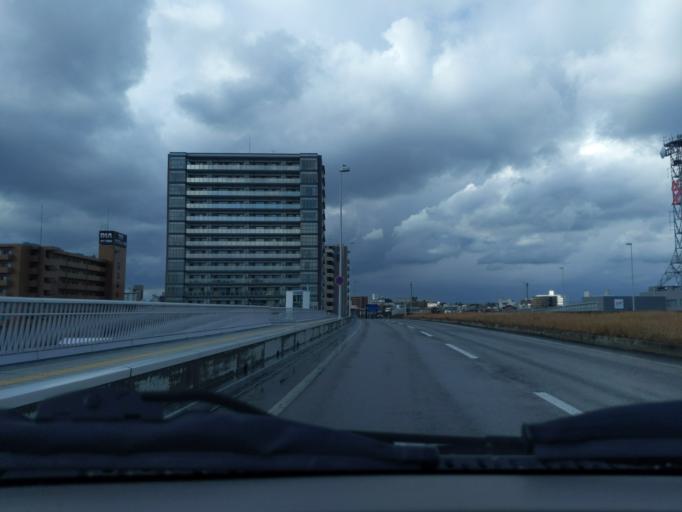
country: JP
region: Niigata
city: Niigata-shi
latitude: 37.9231
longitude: 139.0557
